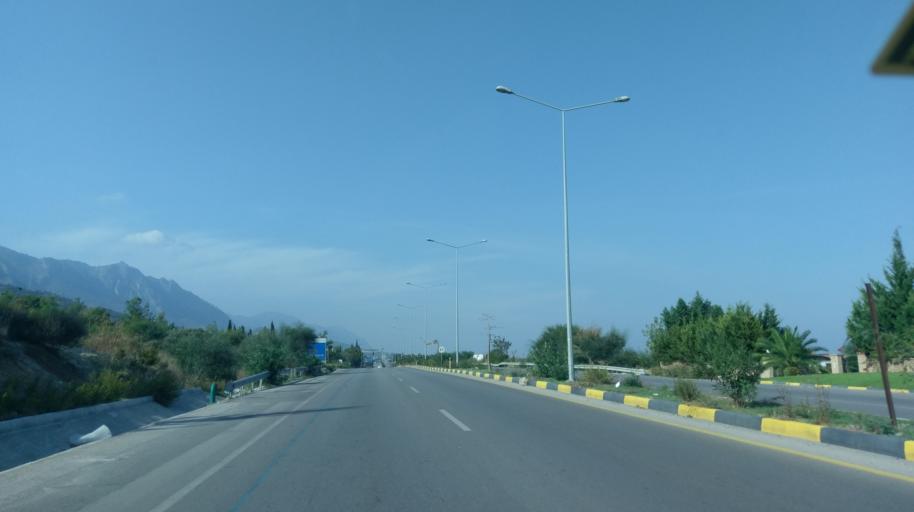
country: CY
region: Keryneia
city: Kyrenia
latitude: 35.3278
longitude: 33.3011
